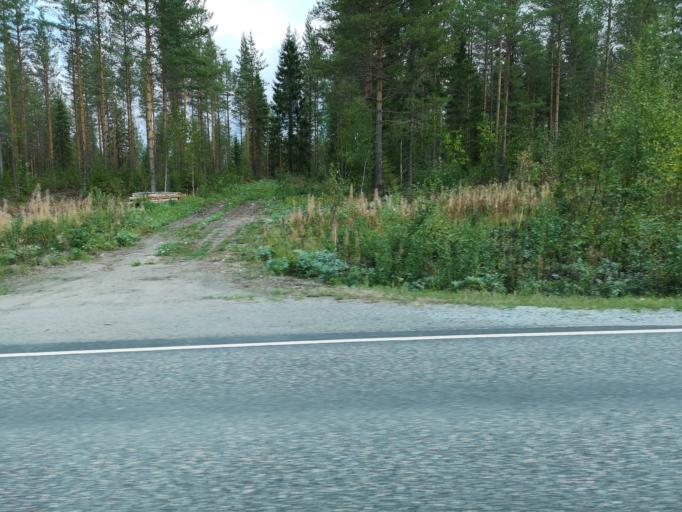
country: FI
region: Central Finland
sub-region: Jyvaeskylae
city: Hankasalmi
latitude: 62.3543
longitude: 26.4557
